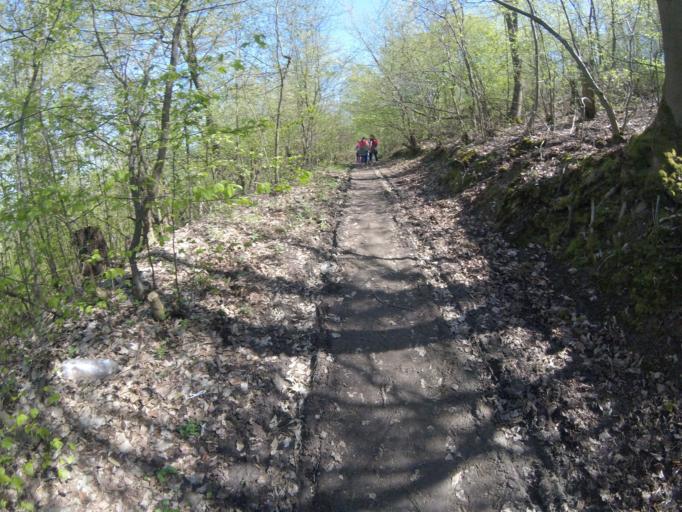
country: HU
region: Borsod-Abauj-Zemplen
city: Szendro
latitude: 48.4085
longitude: 20.7613
